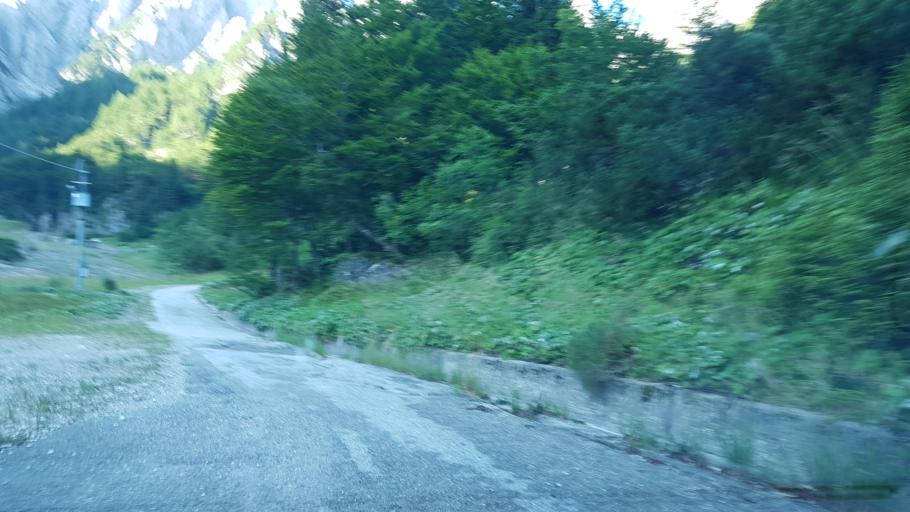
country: IT
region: Friuli Venezia Giulia
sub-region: Provincia di Udine
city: Pontebba
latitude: 46.4843
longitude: 13.2530
